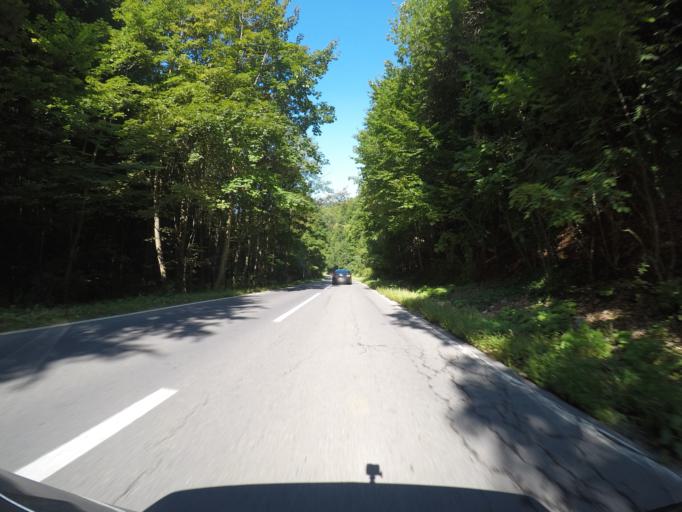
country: RO
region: Brasov
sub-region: Comuna Cristian
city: Cristian
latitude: 45.5862
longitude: 25.5038
